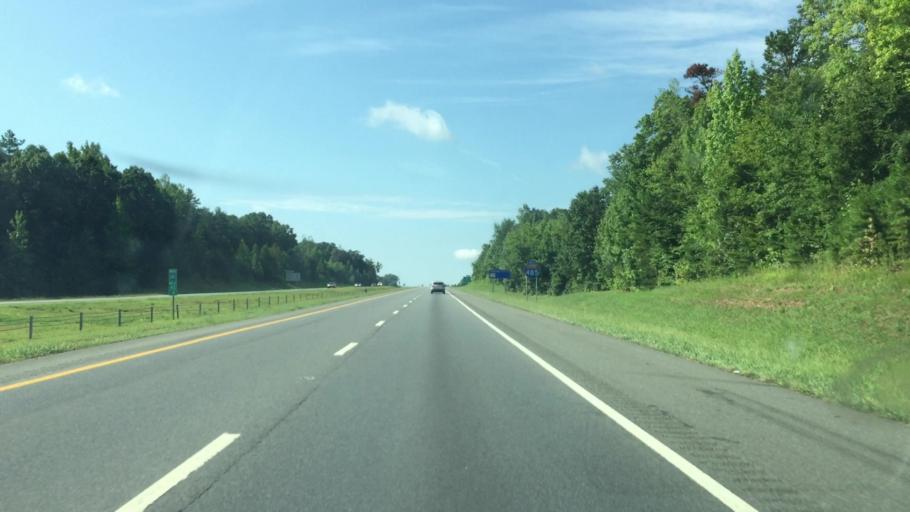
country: US
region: North Carolina
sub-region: Mecklenburg County
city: Mint Hill
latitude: 35.1944
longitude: -80.6294
